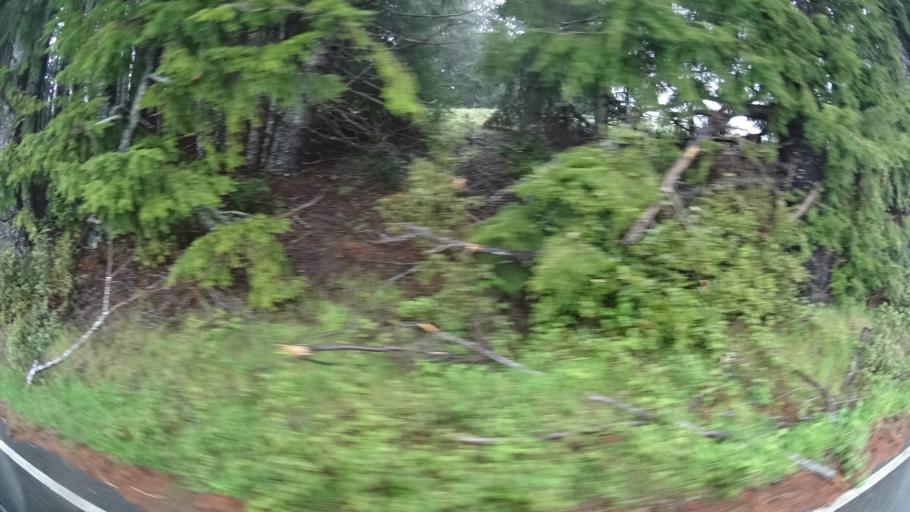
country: US
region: California
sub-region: Humboldt County
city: Westhaven-Moonstone
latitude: 41.1876
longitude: -123.9291
